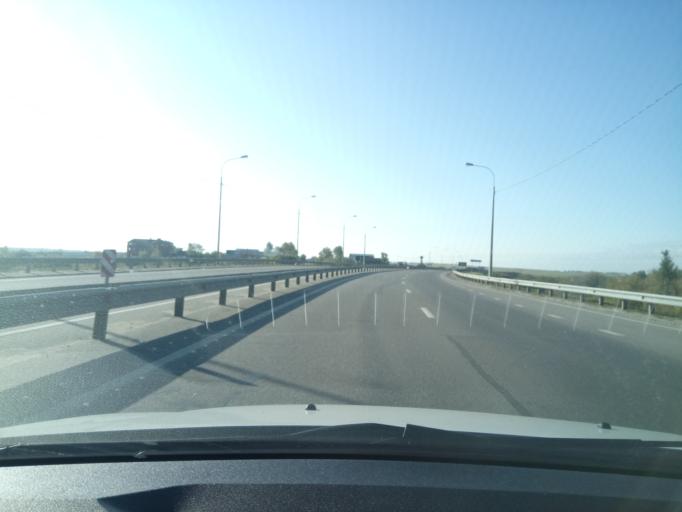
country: RU
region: Nizjnij Novgorod
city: Burevestnik
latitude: 56.1577
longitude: 43.9114
